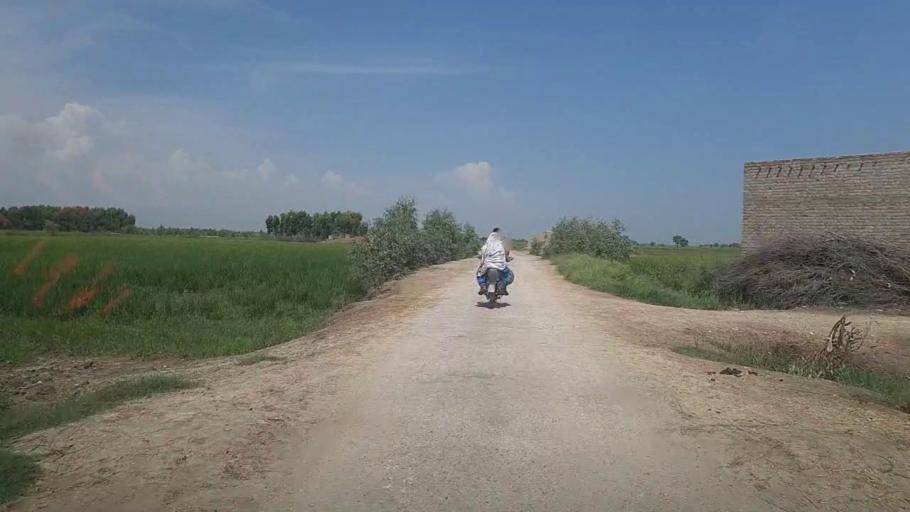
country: PK
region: Sindh
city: Kandhkot
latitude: 28.2877
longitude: 69.2381
